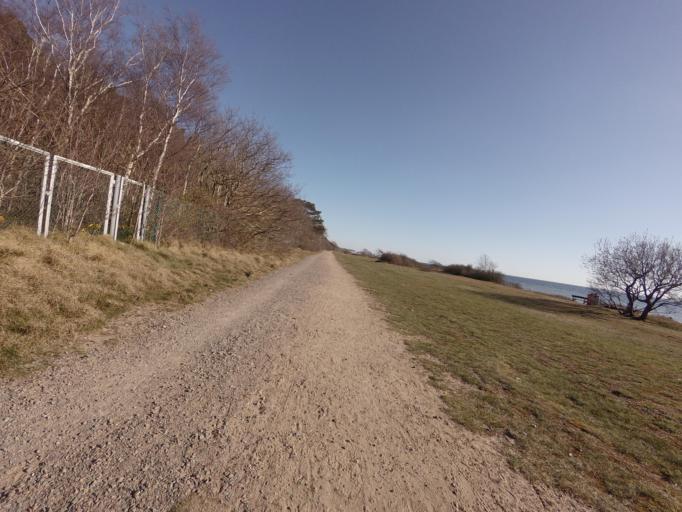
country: SE
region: Skane
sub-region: Helsingborg
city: Helsingborg
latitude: 56.0888
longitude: 12.6493
